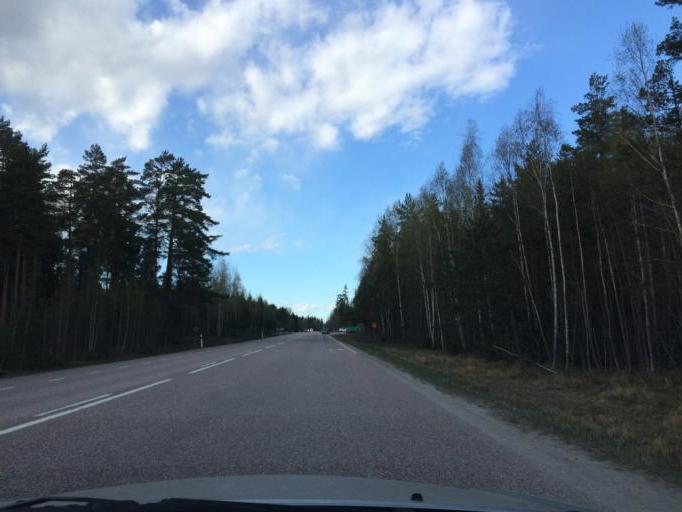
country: SE
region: Vaestmanland
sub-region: Hallstahammars Kommun
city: Kolback
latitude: 59.5770
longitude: 16.3528
